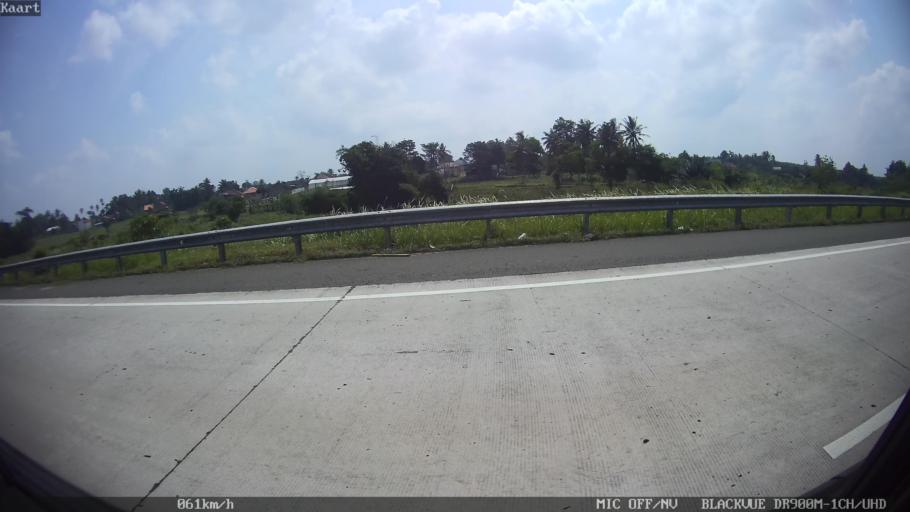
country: ID
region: Lampung
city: Kedaton
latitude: -5.3492
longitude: 105.3211
